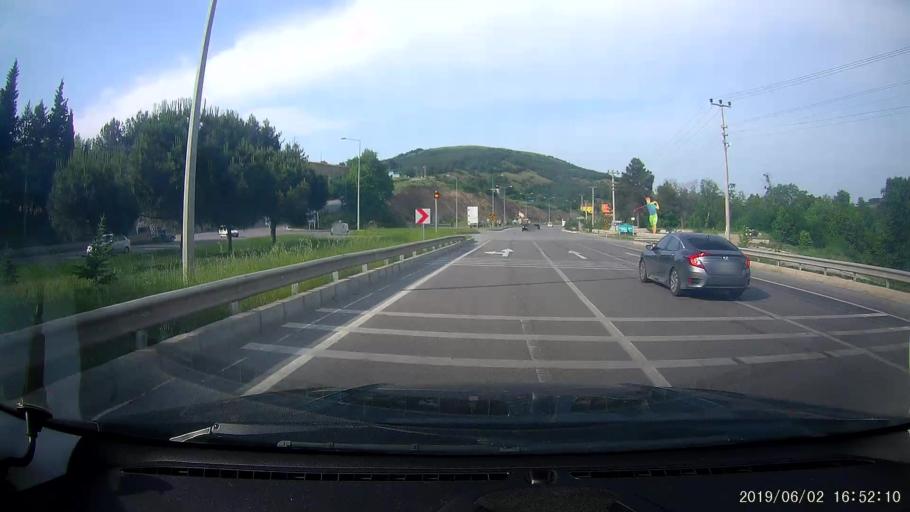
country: TR
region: Samsun
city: Samsun
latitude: 41.2840
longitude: 36.1927
